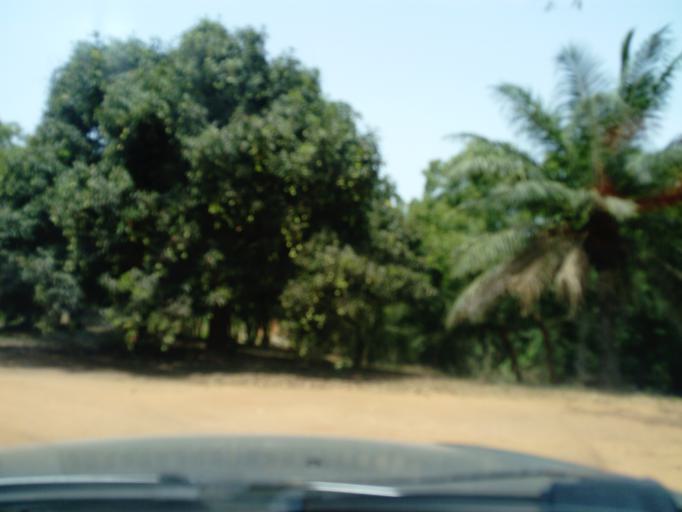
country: GH
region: Central
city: Cape Coast
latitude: 5.1060
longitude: -1.2736
